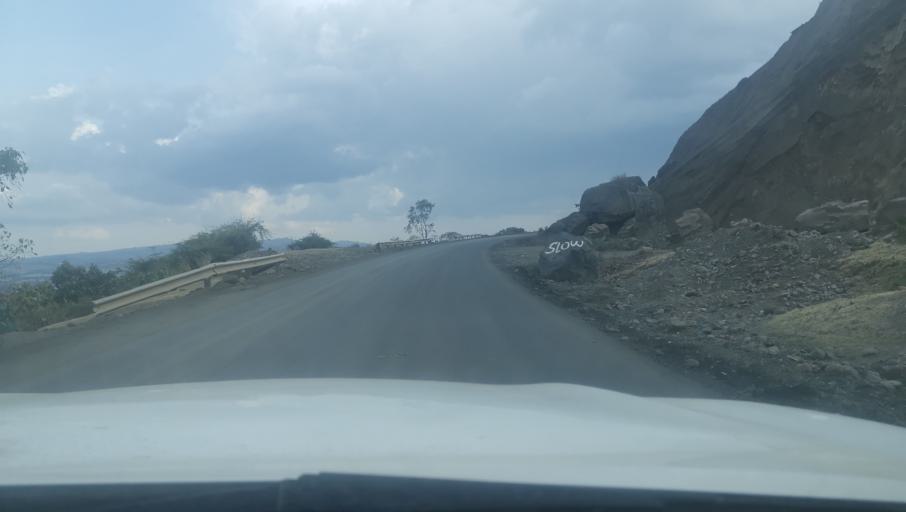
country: ET
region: Oromiya
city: Guder
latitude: 8.9745
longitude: 37.7496
